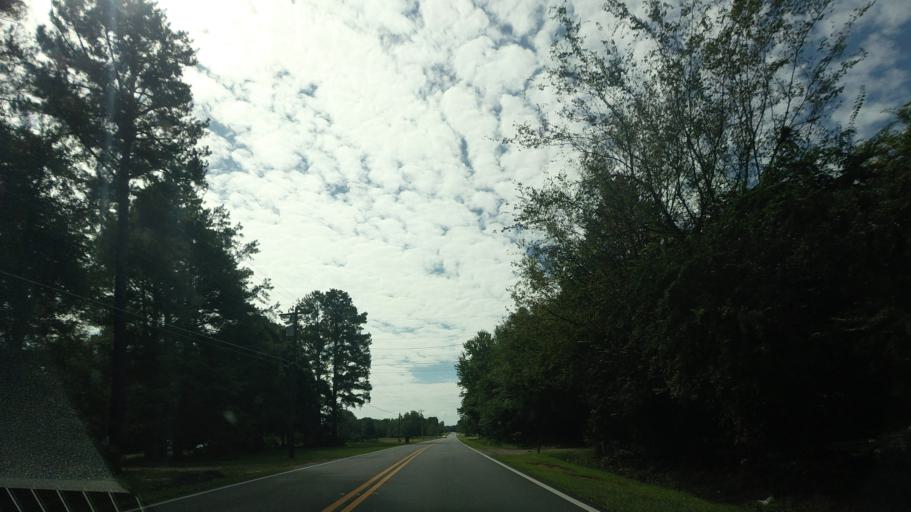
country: US
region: Georgia
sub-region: Houston County
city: Centerville
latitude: 32.6565
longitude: -83.6973
